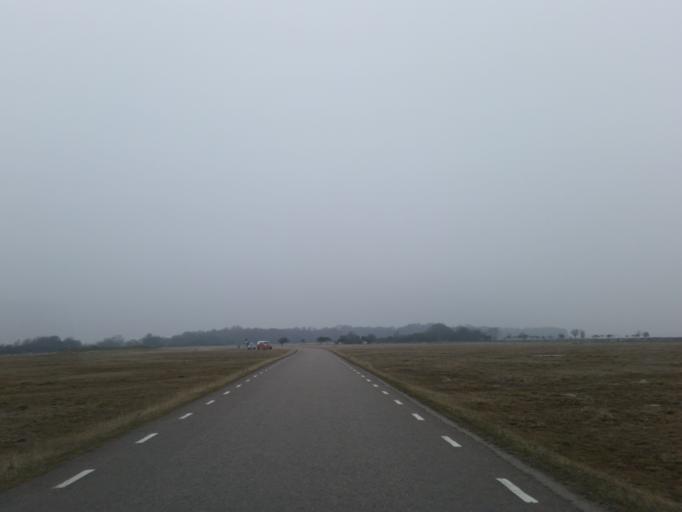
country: SE
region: Kalmar
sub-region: Morbylanga Kommun
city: Moerbylanga
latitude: 56.2079
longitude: 16.4050
